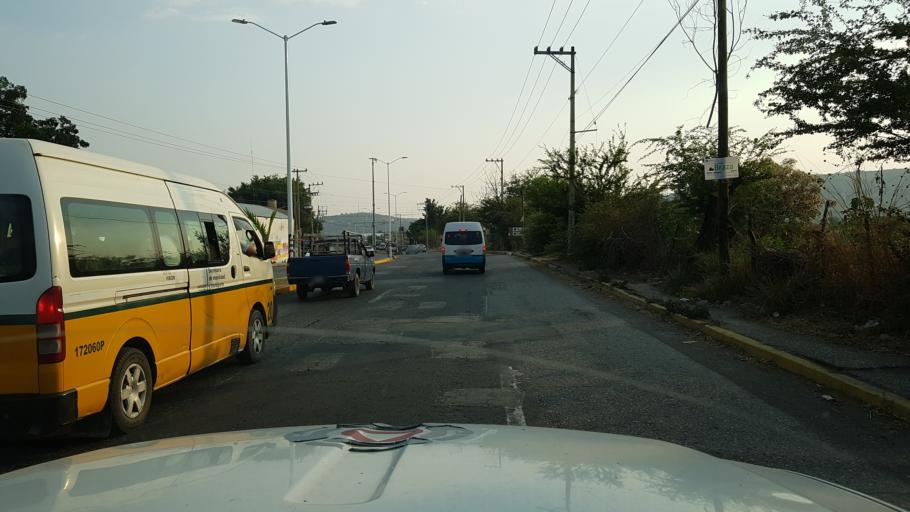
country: MX
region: Morelos
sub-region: Ayala
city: San Pedro Apatlaco
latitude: 18.7938
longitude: -98.9739
